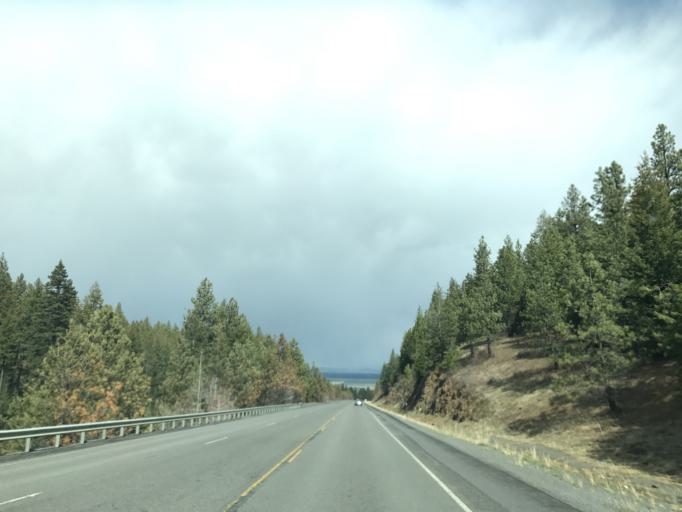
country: US
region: Idaho
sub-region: Idaho County
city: Grangeville
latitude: 45.8578
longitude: -116.2371
